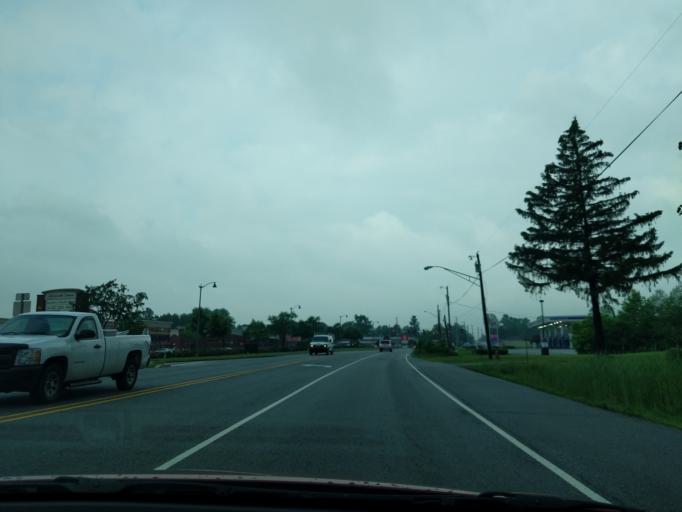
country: US
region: Indiana
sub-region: Hancock County
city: McCordsville
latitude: 39.8972
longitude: -85.9169
